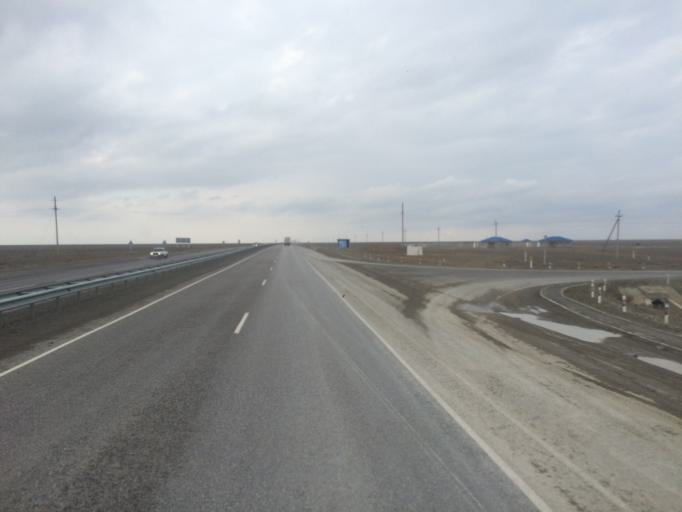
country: KZ
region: Qyzylorda
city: Shalqiya
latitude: 43.6060
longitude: 67.6714
